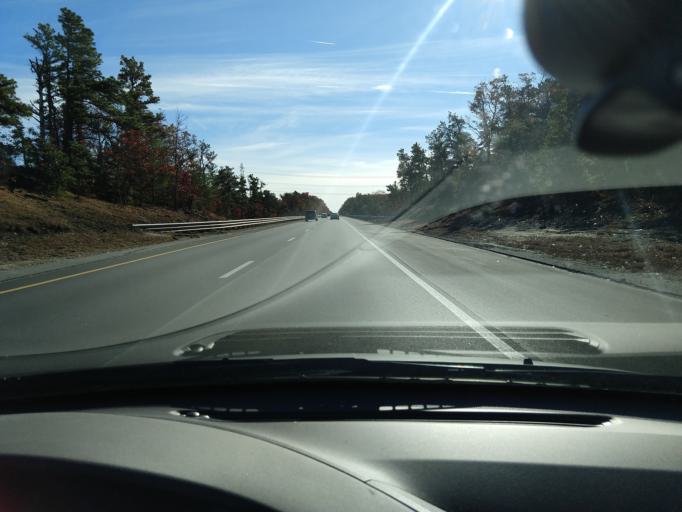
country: US
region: Massachusetts
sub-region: Plymouth County
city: Plymouth
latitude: 41.9121
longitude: -70.6200
